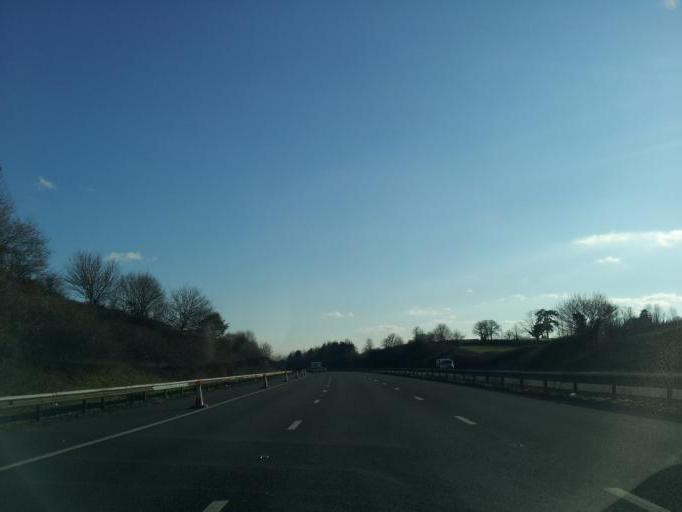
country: GB
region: England
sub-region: Devon
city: Bradninch
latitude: 50.7965
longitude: -3.4436
